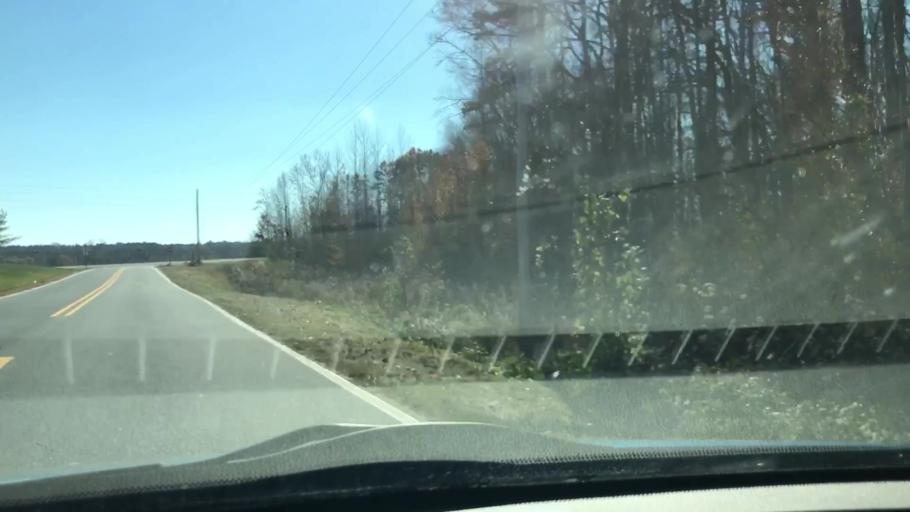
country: US
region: North Carolina
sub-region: Davidson County
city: Denton
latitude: 35.6409
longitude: -79.9723
